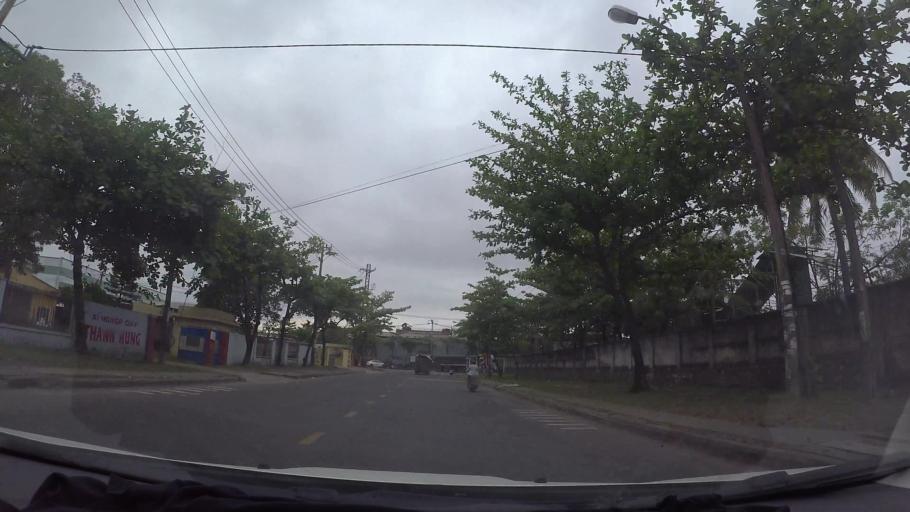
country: VN
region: Da Nang
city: Lien Chieu
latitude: 16.0834
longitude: 108.1396
